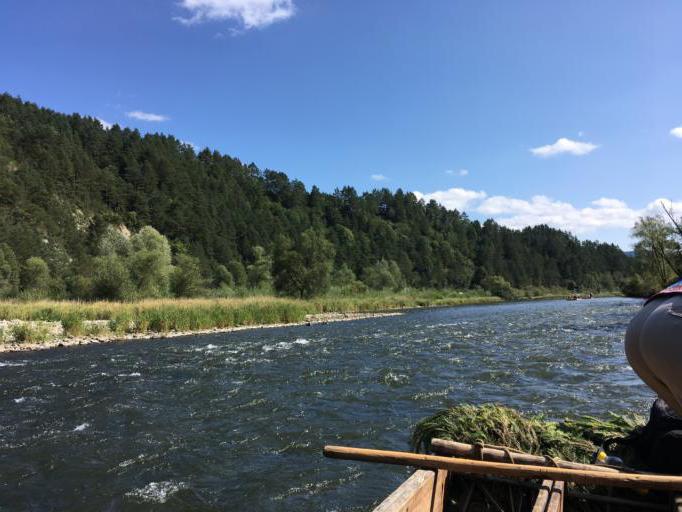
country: PL
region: Lesser Poland Voivodeship
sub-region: Powiat nowotarski
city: Krosnica
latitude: 49.4058
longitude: 20.3787
